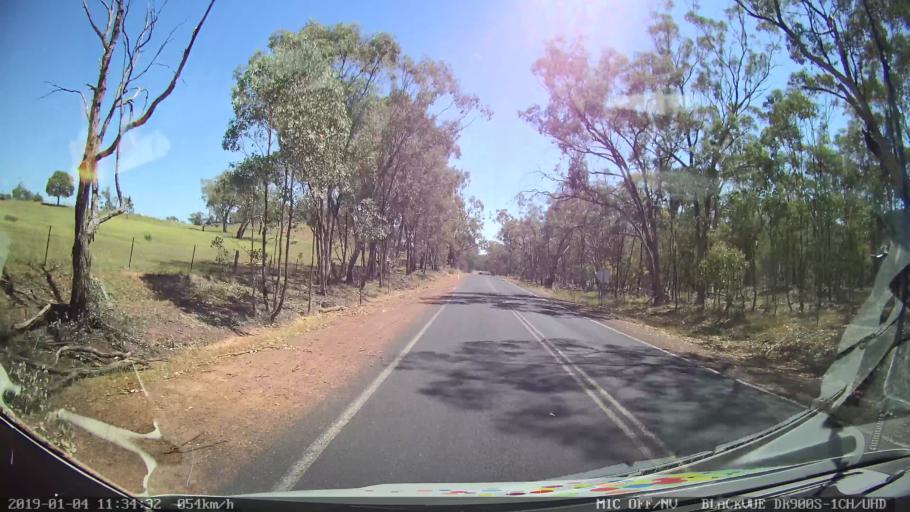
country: AU
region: New South Wales
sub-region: Cabonne
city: Molong
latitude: -33.0657
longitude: 148.8250
